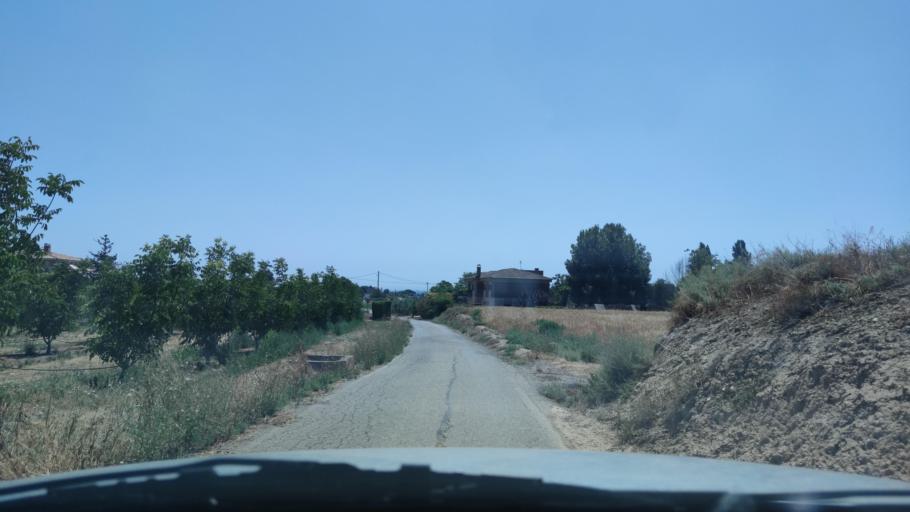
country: ES
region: Catalonia
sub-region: Provincia de Lleida
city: Torrefarrera
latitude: 41.6485
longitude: 0.5858
